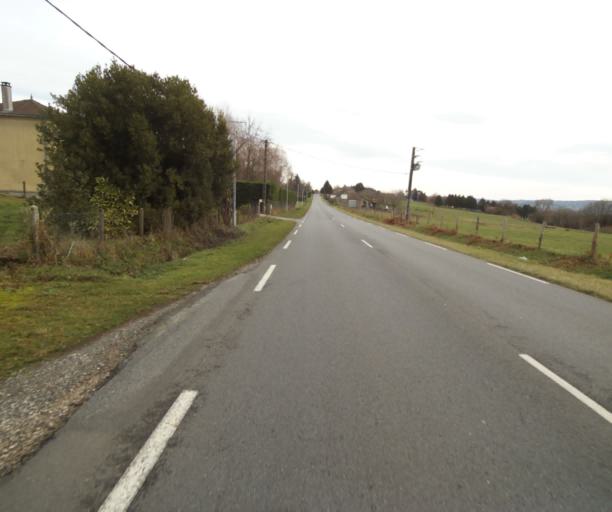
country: FR
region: Limousin
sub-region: Departement de la Correze
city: Chameyrat
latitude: 45.2682
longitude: 1.7025
